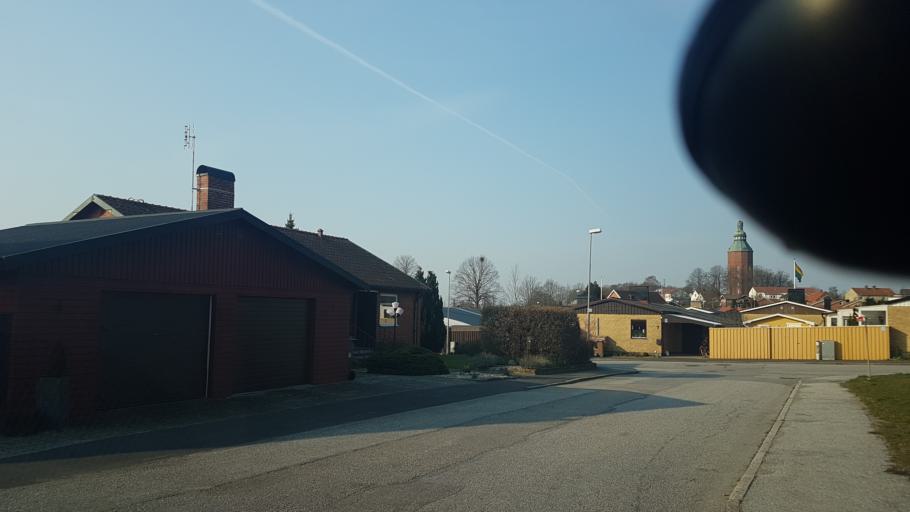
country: SE
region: Skane
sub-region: Ystads Kommun
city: Ystad
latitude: 55.4408
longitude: 13.8335
